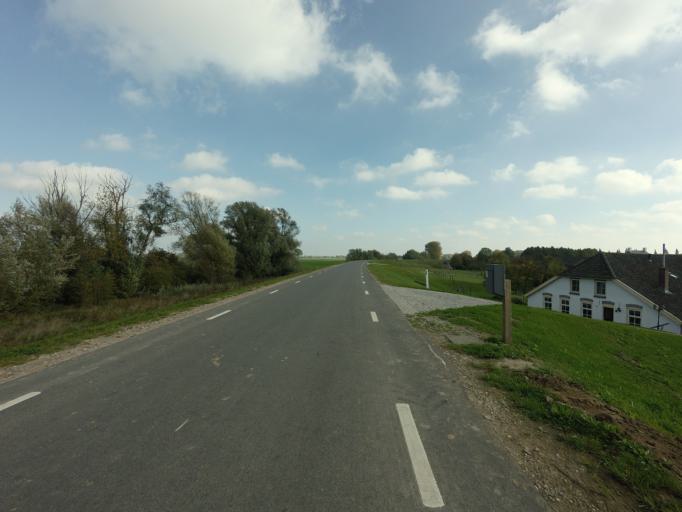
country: NL
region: Utrecht
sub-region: Gemeente Wijk bij Duurstede
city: Wijk bij Duurstede
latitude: 51.9564
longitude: 5.2868
